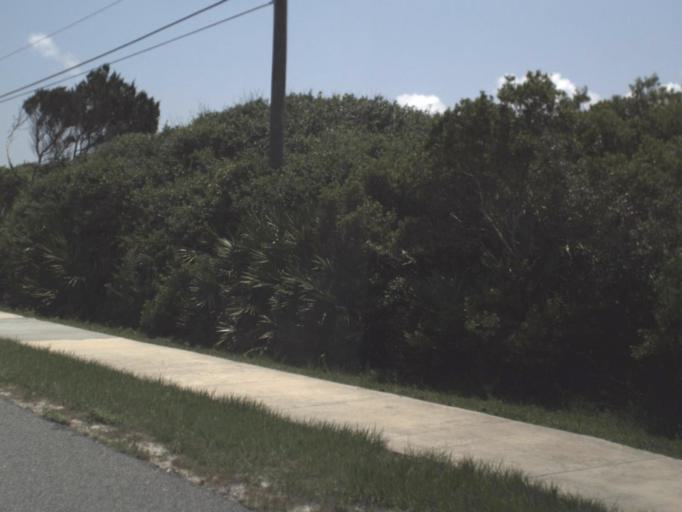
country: US
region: Florida
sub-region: Saint Johns County
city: Butler Beach
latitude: 29.7204
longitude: -81.2351
